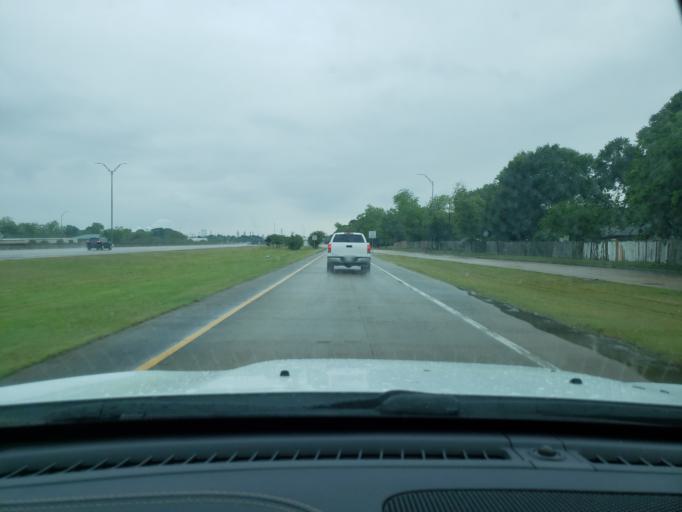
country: US
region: Texas
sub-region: Harris County
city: Baytown
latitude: 29.7504
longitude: -94.9676
